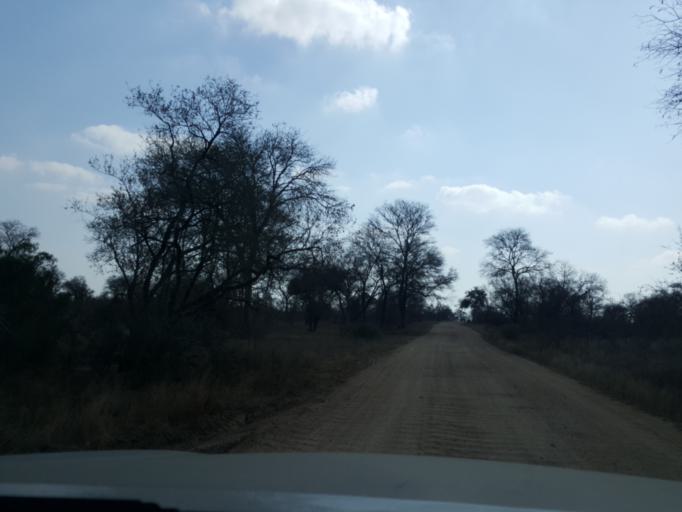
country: ZA
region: Mpumalanga
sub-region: Ehlanzeni District
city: Komatipoort
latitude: -25.2685
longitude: 31.7991
